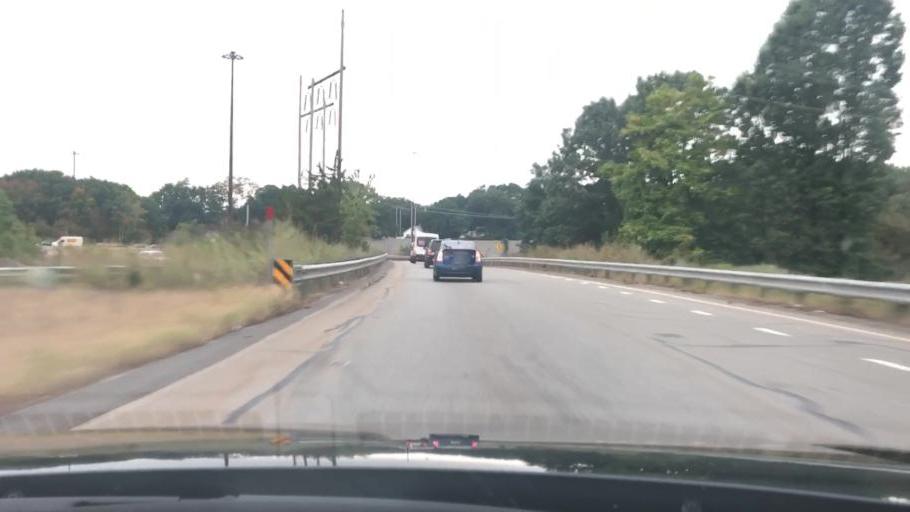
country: US
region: Massachusetts
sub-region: Middlesex County
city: Lowell
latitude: 42.6087
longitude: -71.3243
